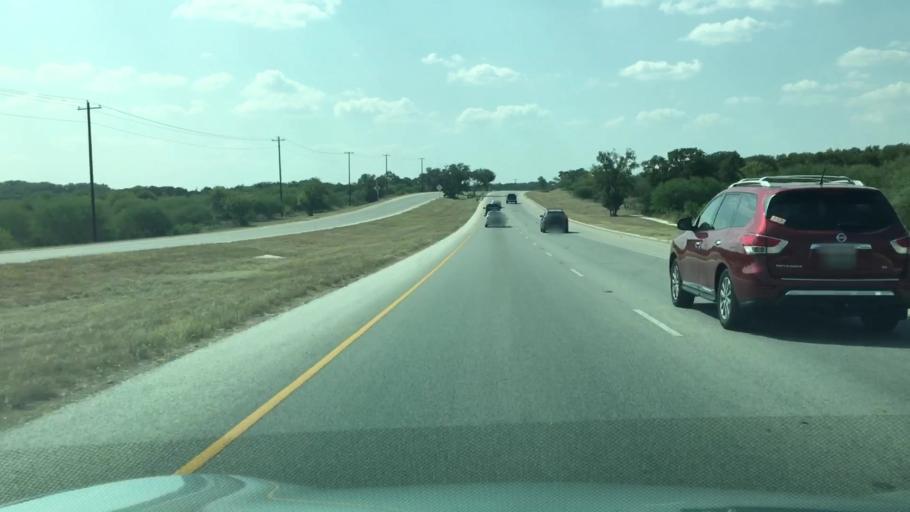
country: US
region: Texas
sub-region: Hays County
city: San Marcos
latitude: 29.8823
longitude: -97.9742
